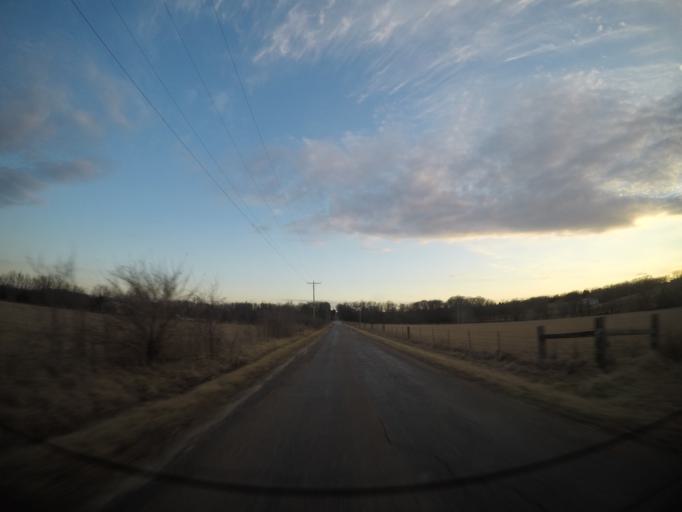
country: US
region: Kansas
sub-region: Wyandotte County
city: Bonner Springs
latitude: 39.0326
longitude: -94.9089
